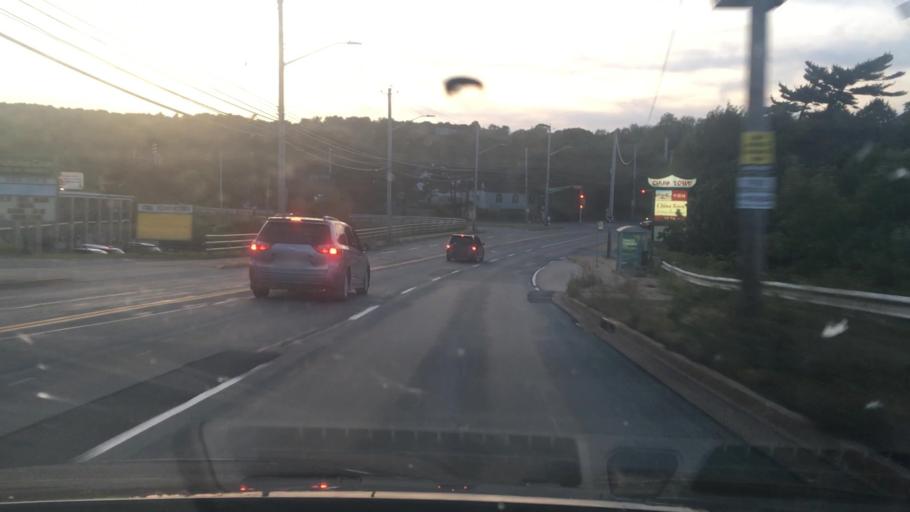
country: CA
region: Nova Scotia
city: Dartmouth
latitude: 44.6815
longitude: -63.6591
